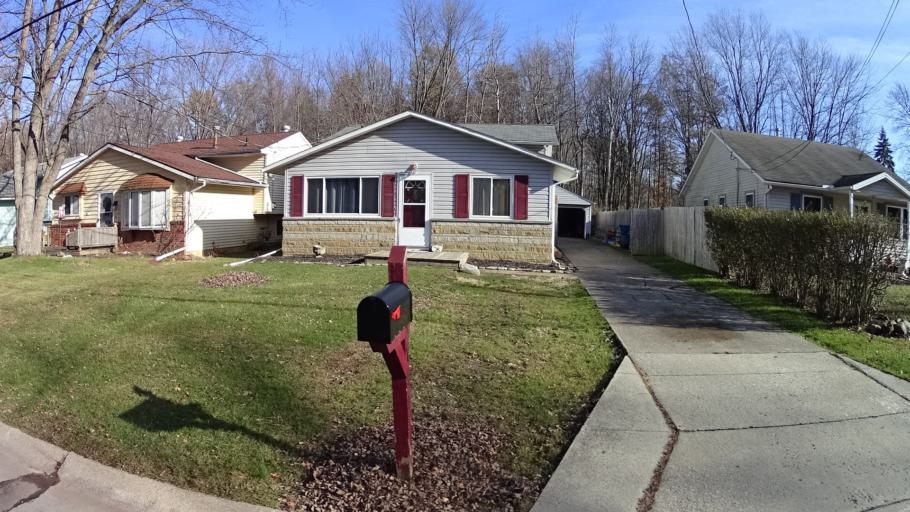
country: US
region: Ohio
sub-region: Lorain County
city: North Ridgeville
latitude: 41.4066
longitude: -81.9858
